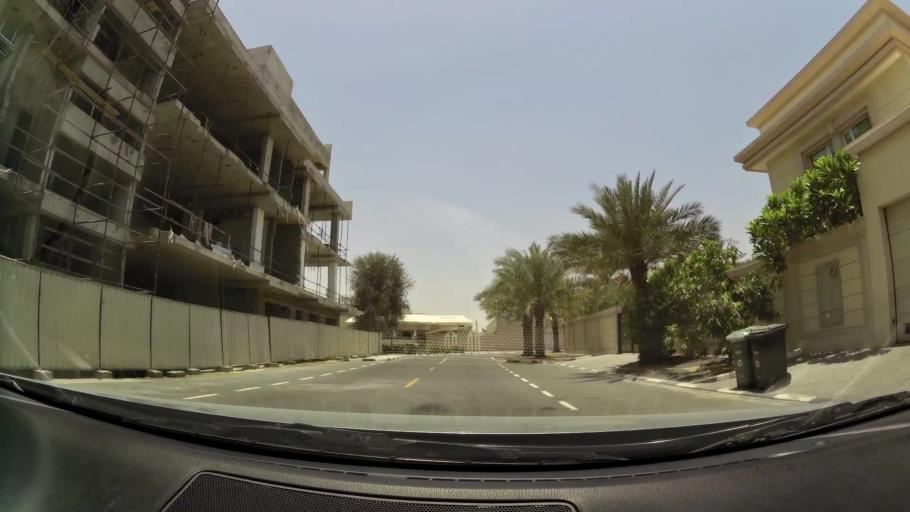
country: AE
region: Dubai
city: Dubai
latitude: 25.1664
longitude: 55.2348
